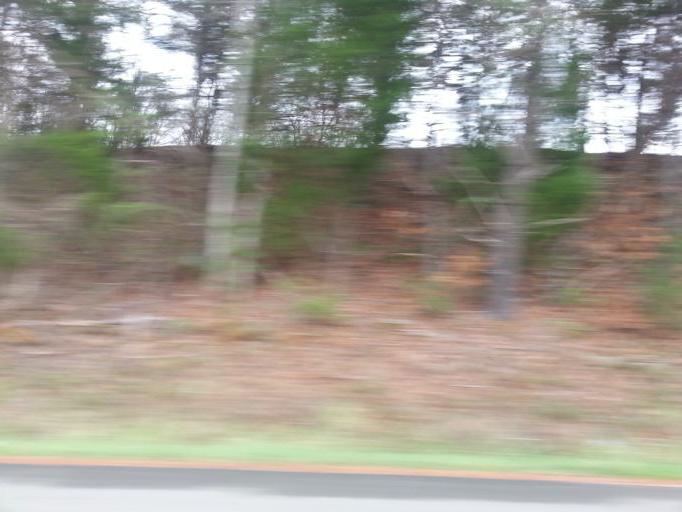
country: US
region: Tennessee
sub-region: Greene County
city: Mosheim
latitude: 36.0762
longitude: -82.9620
